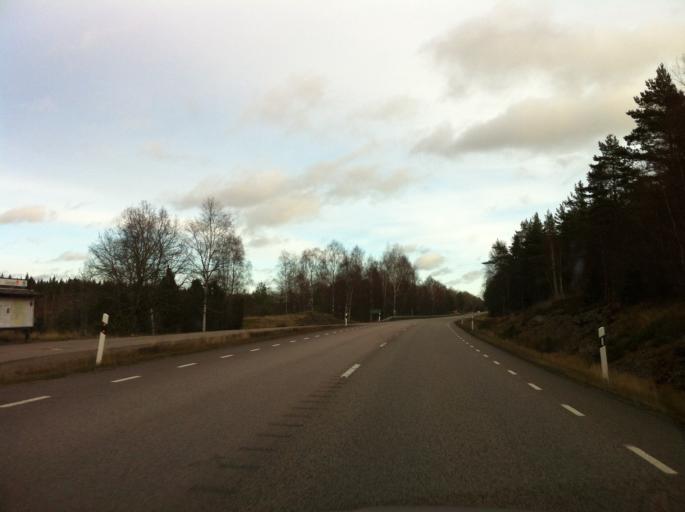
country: SE
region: Kronoberg
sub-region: Uppvidinge Kommun
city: Aseda
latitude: 57.1375
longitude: 15.2823
